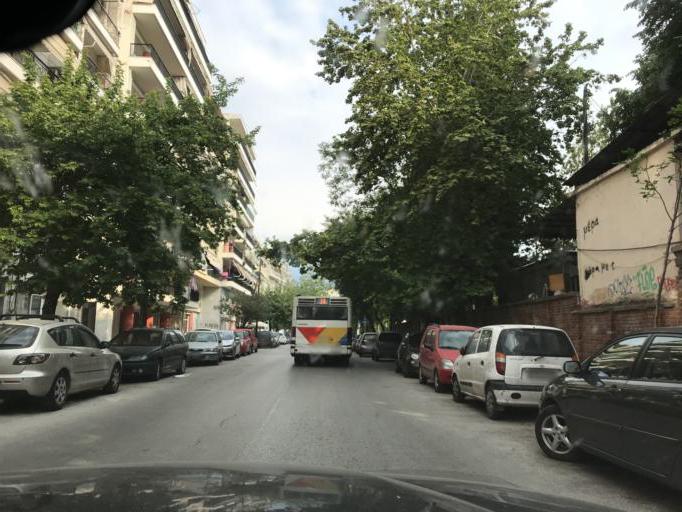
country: GR
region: Central Macedonia
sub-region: Nomos Thessalonikis
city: Thessaloniki
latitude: 40.6460
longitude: 22.9287
